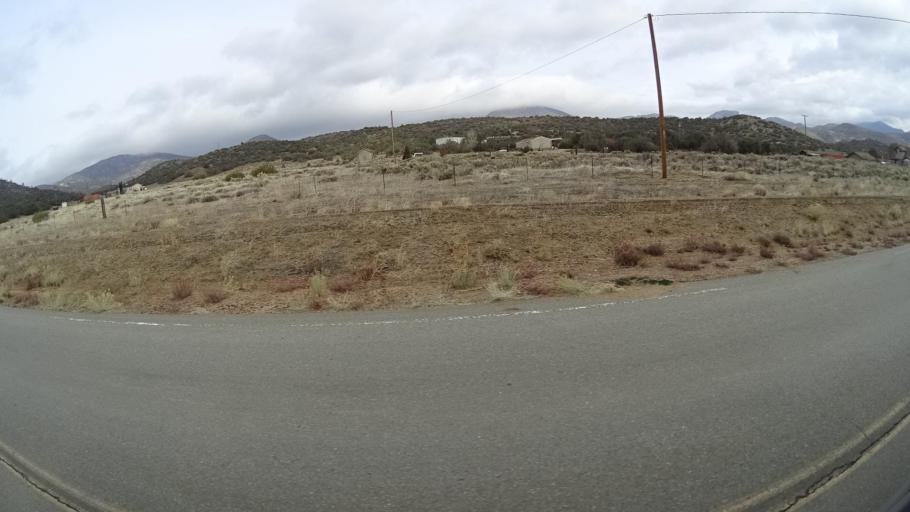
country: US
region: California
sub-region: Kern County
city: Tehachapi
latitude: 35.1744
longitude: -118.3528
